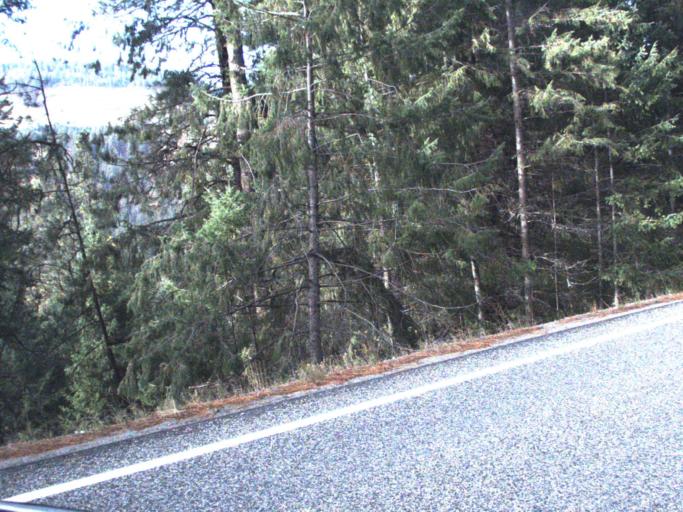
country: US
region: Washington
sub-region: Stevens County
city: Kettle Falls
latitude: 48.8041
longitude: -118.0041
